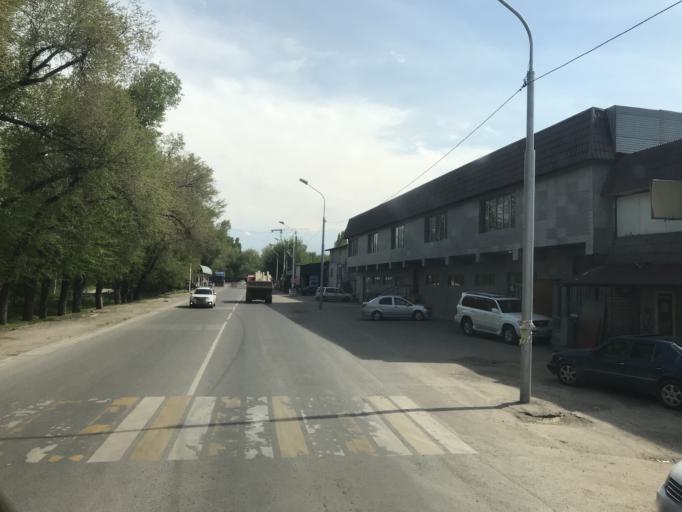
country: KZ
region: Almaty Qalasy
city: Almaty
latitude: 43.2416
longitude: 76.8055
